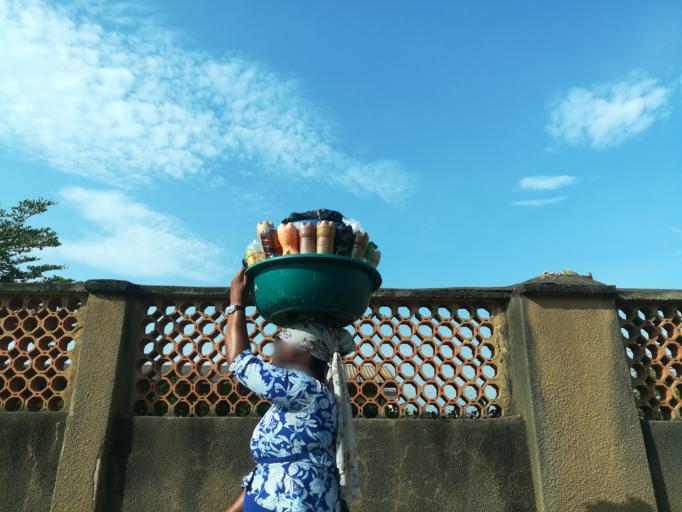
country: NG
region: Lagos
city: Ojota
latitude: 6.6013
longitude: 3.4199
